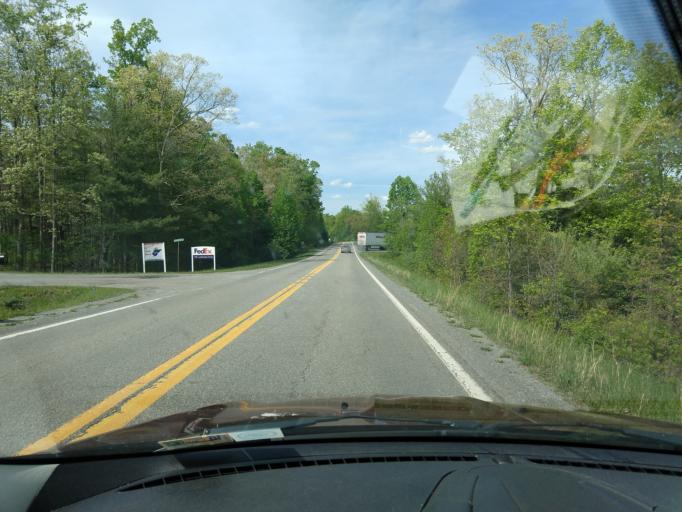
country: US
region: West Virginia
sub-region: Raleigh County
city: Stanaford
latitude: 37.7926
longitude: -81.1173
